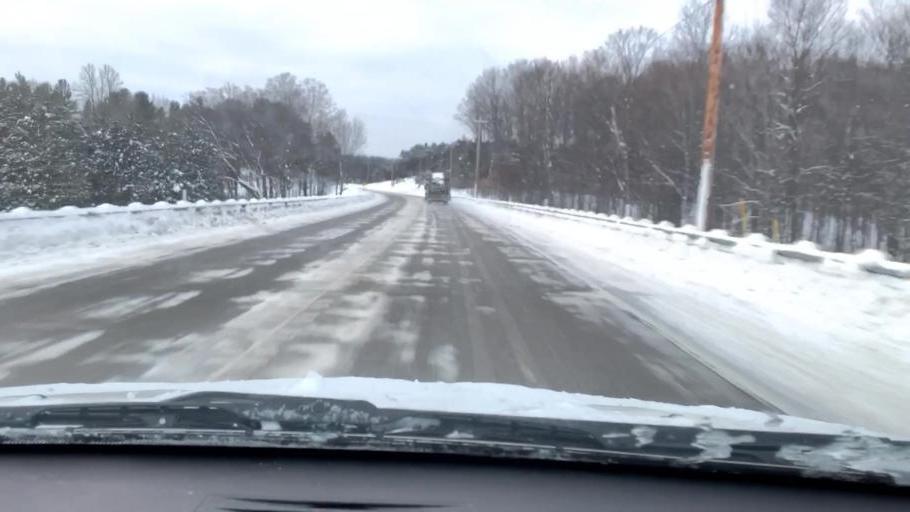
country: US
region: Michigan
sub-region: Wexford County
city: Manton
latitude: 44.5819
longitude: -85.3601
